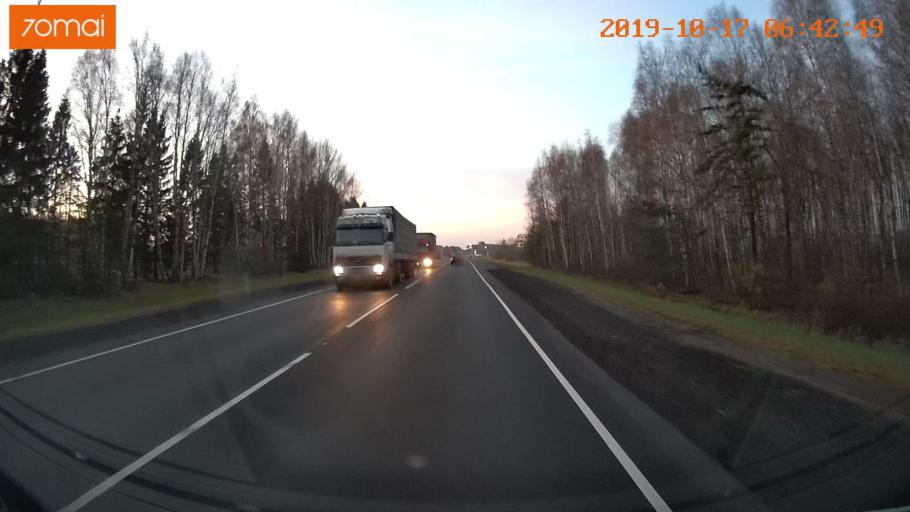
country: RU
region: Vladimir
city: Kideksha
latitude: 56.5960
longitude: 40.5556
